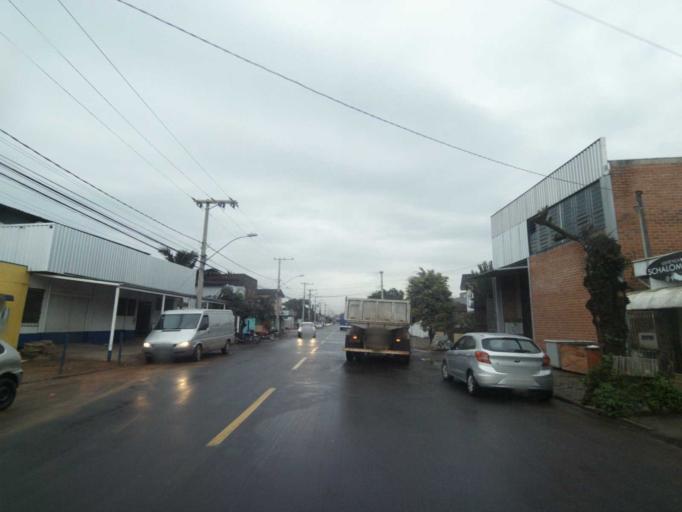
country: BR
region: Rio Grande do Sul
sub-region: Sao Leopoldo
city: Sao Leopoldo
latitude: -29.7717
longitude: -51.1555
